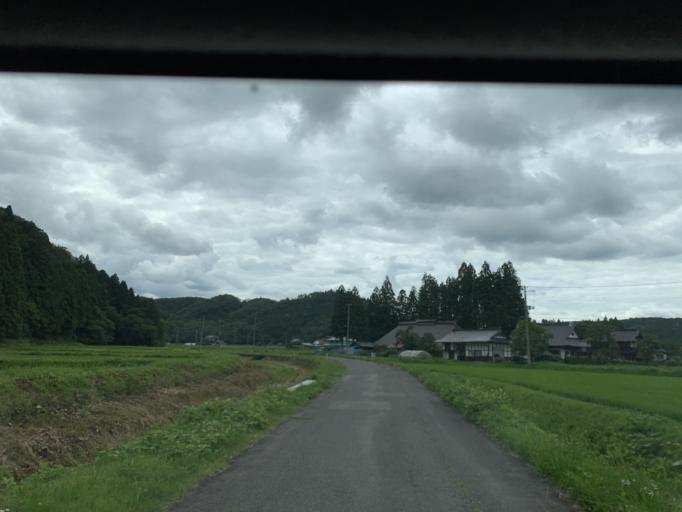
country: JP
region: Iwate
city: Ichinoseki
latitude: 38.9483
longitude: 141.0166
